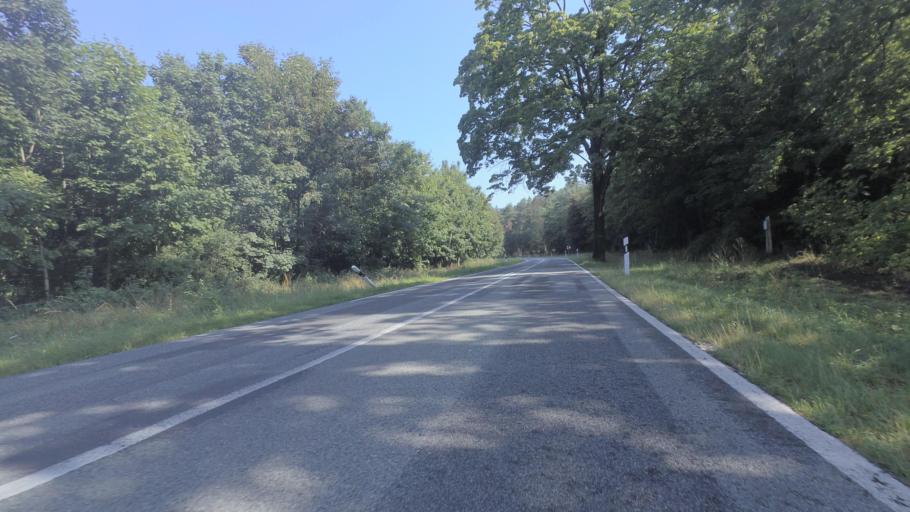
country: DE
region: Mecklenburg-Vorpommern
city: Malchow
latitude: 53.5871
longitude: 12.4699
